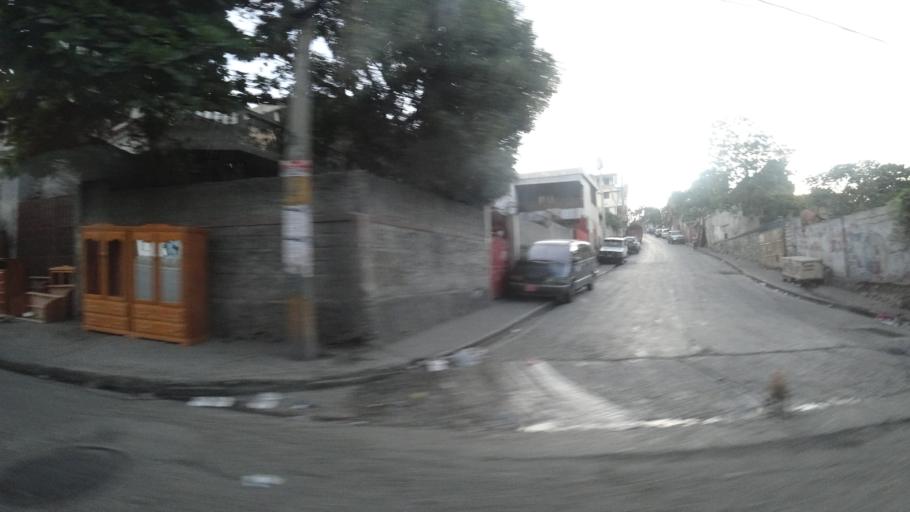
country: HT
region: Ouest
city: Delmas 73
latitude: 18.5472
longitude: -72.3173
